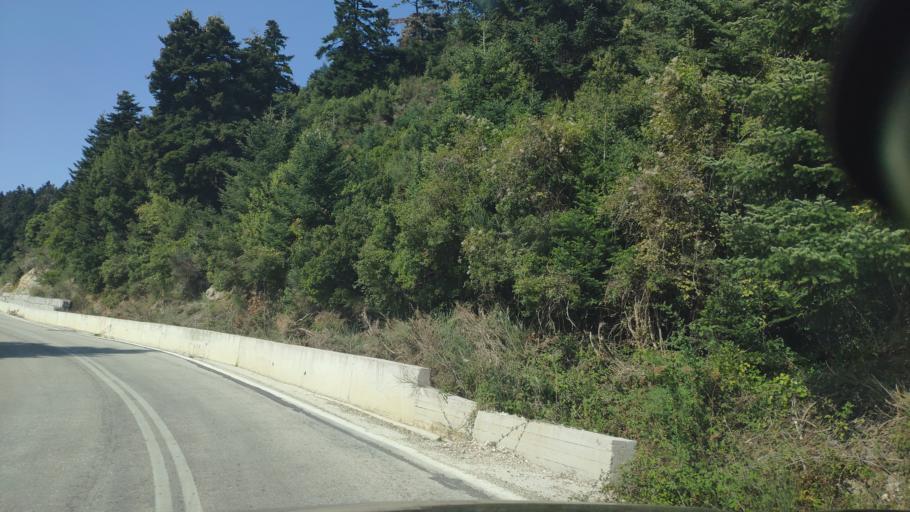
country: GR
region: West Greece
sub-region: Nomos Achaias
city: Aiyira
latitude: 37.8676
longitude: 22.3774
